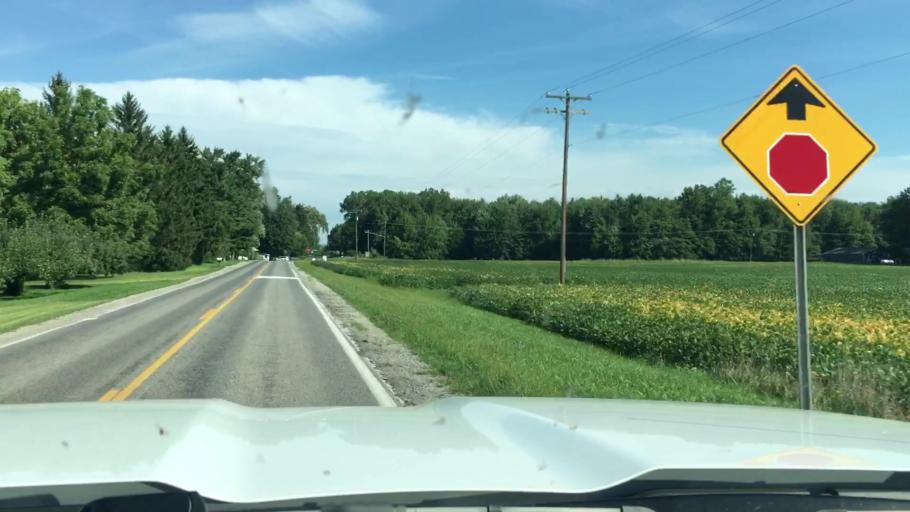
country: US
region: Michigan
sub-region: Saginaw County
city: Hemlock
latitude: 43.4797
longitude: -84.2303
